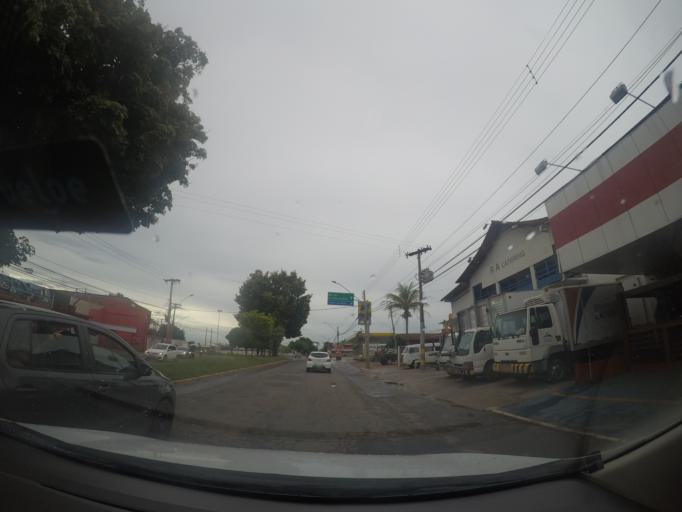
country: BR
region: Goias
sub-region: Goiania
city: Goiania
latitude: -16.6343
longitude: -49.2369
